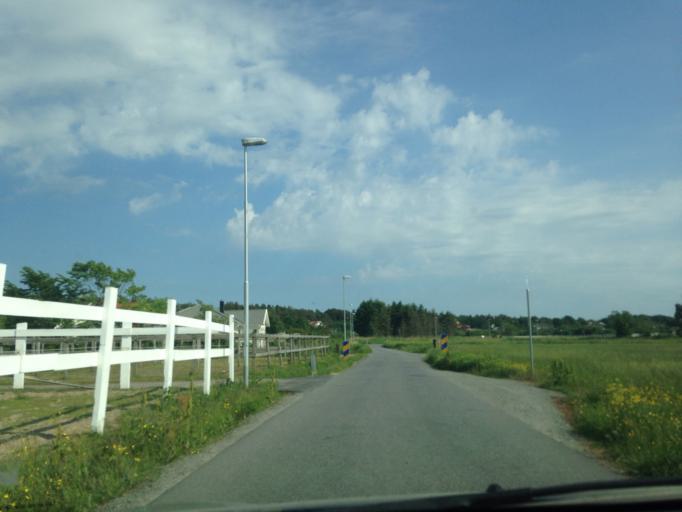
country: SE
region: Vaestra Goetaland
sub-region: Goteborg
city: Torslanda
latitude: 57.7768
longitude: 11.8298
